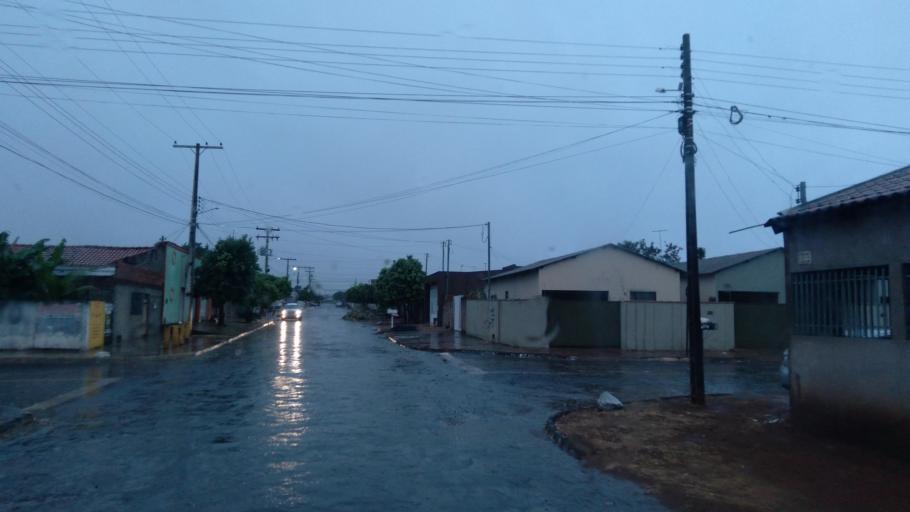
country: BR
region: Goias
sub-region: Mineiros
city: Mineiros
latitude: -17.5417
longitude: -52.5458
